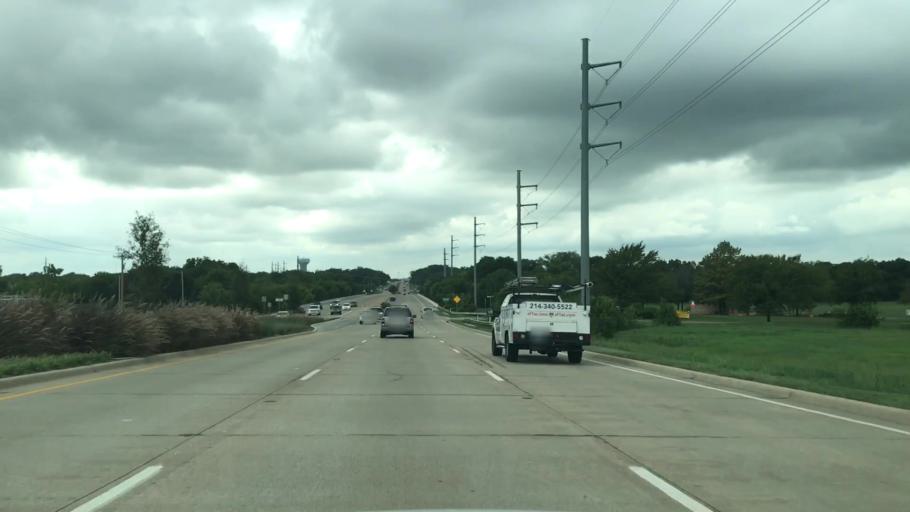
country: US
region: Texas
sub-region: Dallas County
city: Rowlett
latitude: 32.9091
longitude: -96.5881
